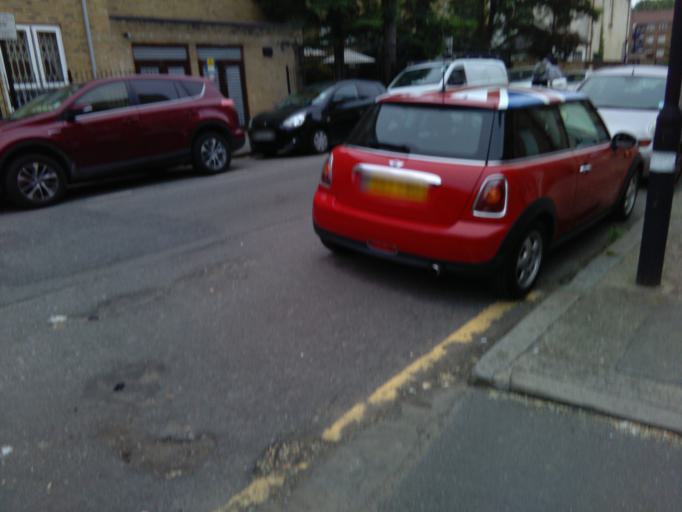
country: GB
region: England
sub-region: Greater London
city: Brixton
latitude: 51.4691
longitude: -0.1139
